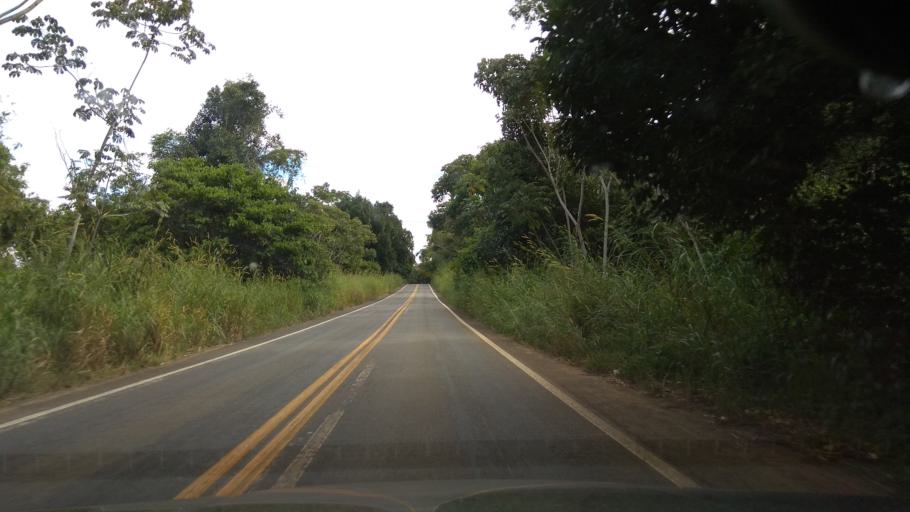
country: BR
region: Bahia
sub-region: Ubata
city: Ubata
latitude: -14.2285
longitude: -39.4827
